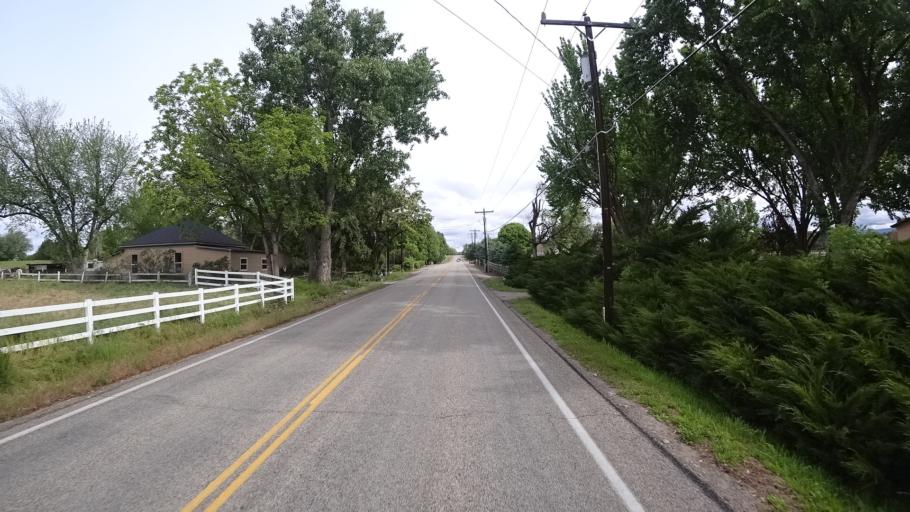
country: US
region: Idaho
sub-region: Ada County
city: Eagle
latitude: 43.7125
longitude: -116.3540
